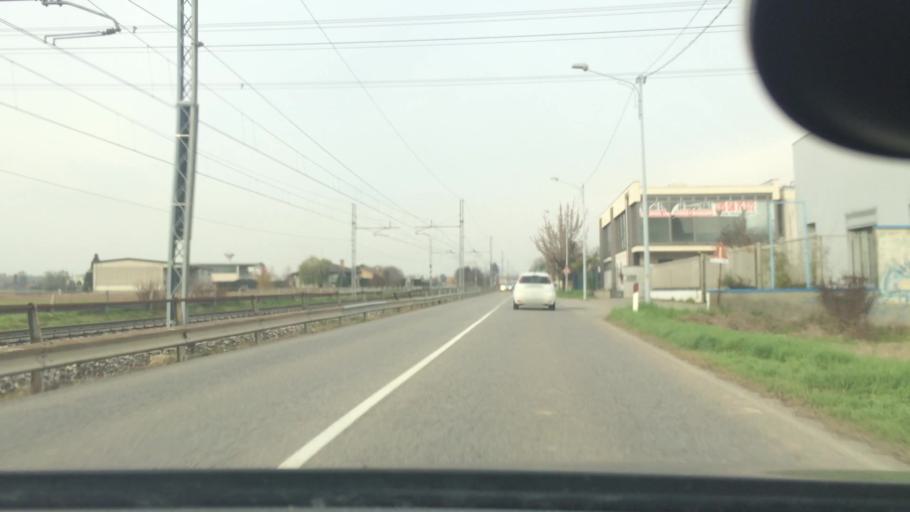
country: IT
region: Lombardy
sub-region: Provincia di Como
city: Rovello Porro
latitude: 45.6592
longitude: 9.0379
